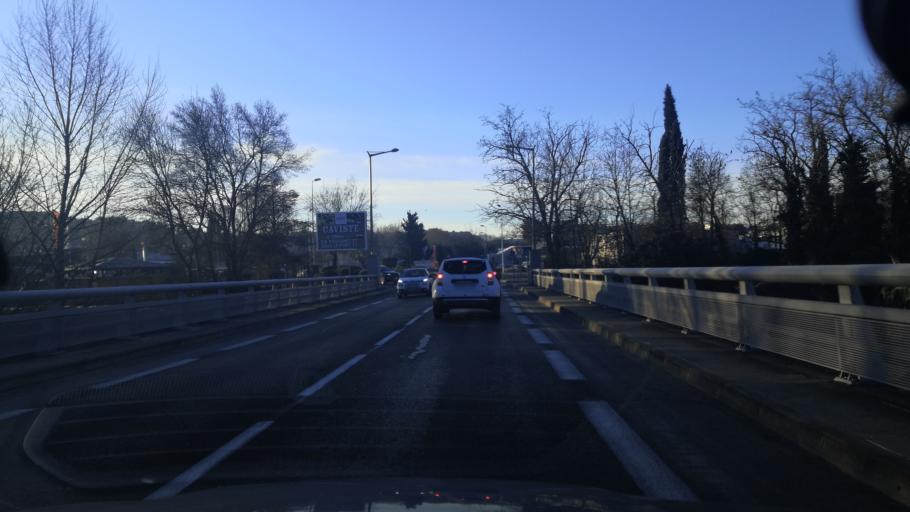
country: FR
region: Provence-Alpes-Cote d'Azur
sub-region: Departement des Bouches-du-Rhone
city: Aix-en-Provence
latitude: 43.5090
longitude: 5.4088
